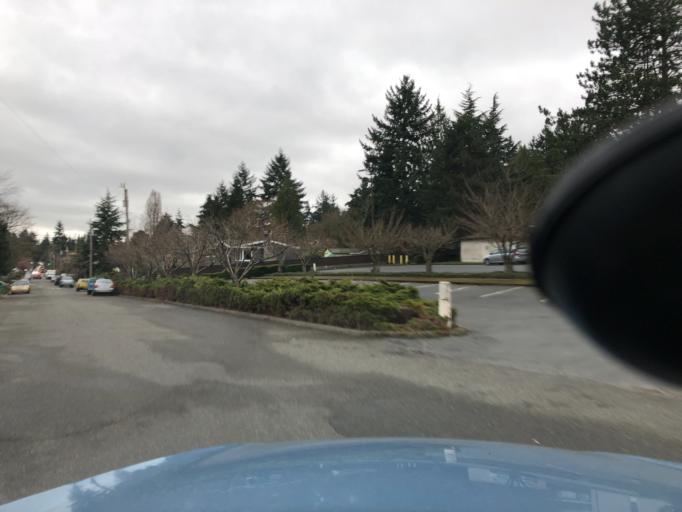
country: US
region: Washington
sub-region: King County
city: Lake Forest Park
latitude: 47.7369
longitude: -122.2964
